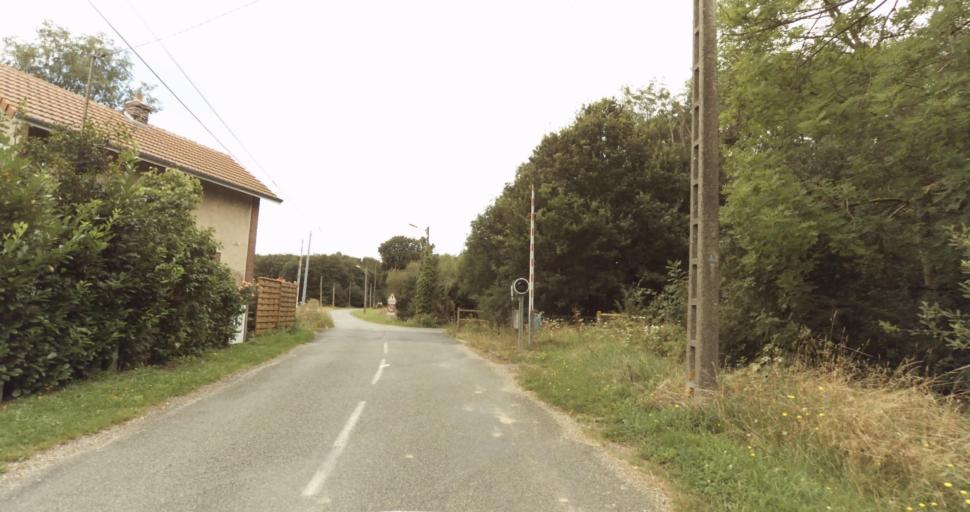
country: FR
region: Haute-Normandie
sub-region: Departement de l'Eure
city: Evreux
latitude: 48.9414
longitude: 1.1899
